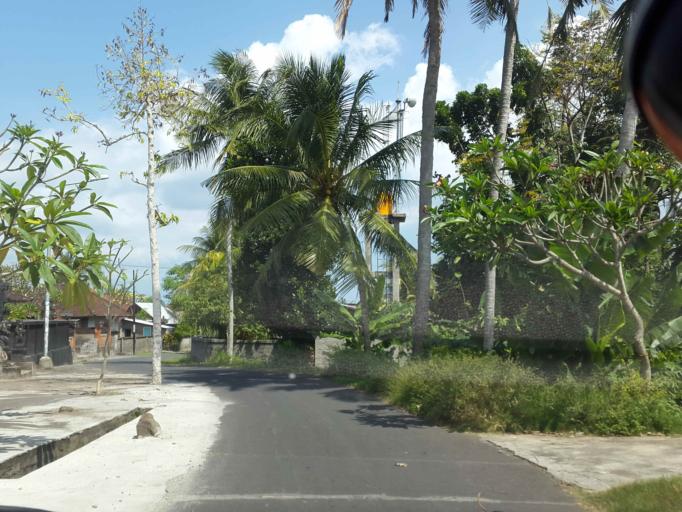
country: ID
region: Bali
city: Klungkung
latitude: -8.5562
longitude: 115.3802
